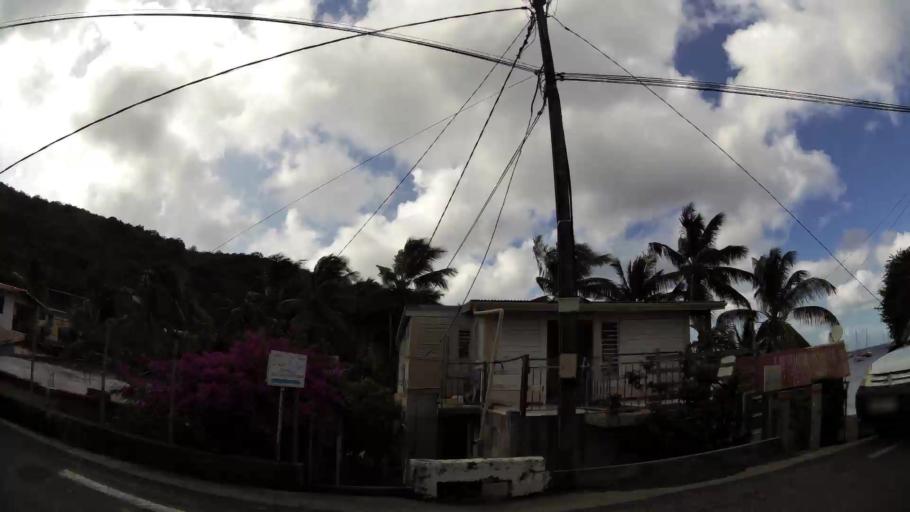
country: MQ
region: Martinique
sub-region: Martinique
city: Les Trois-Ilets
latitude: 14.4996
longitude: -61.0835
